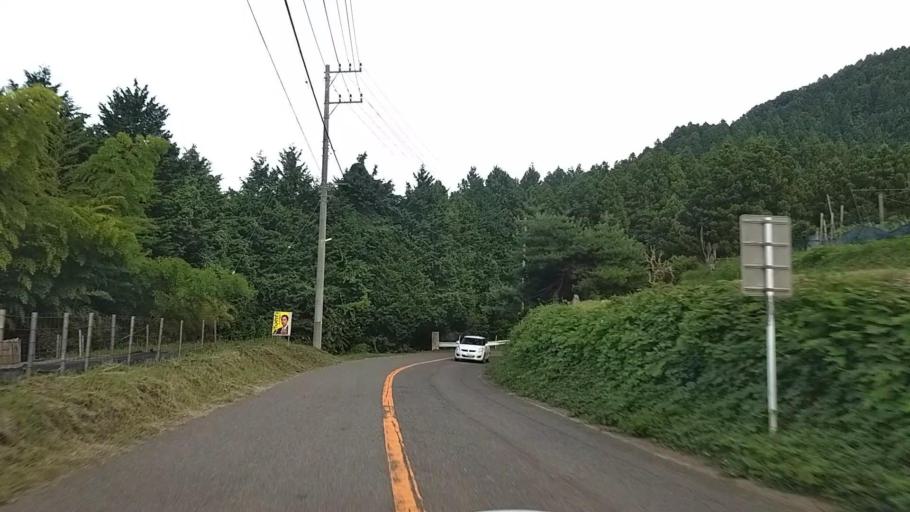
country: JP
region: Yamanashi
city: Uenohara
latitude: 35.6127
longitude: 139.2092
